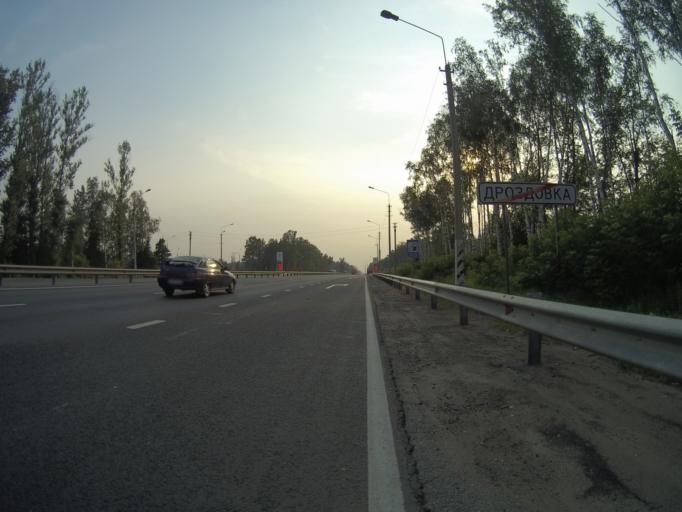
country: RU
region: Vladimir
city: Novki
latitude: 56.2016
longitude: 41.0990
